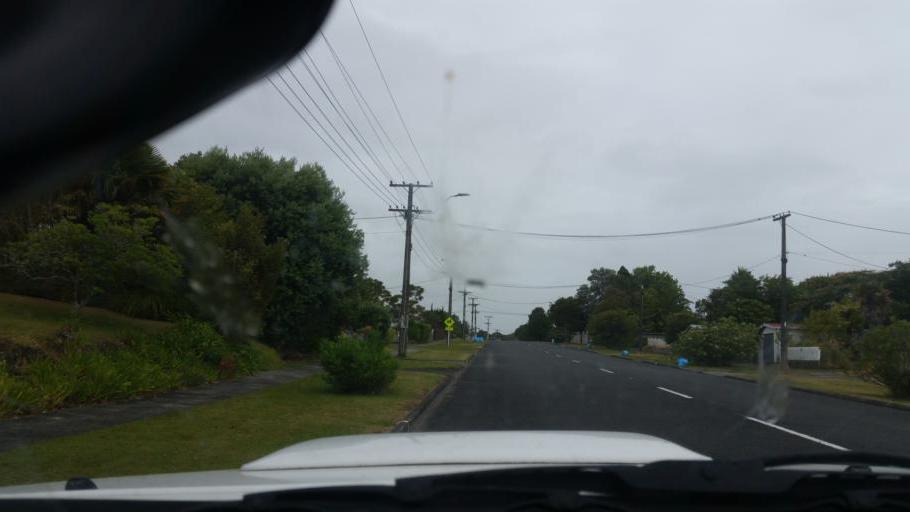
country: NZ
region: Northland
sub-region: Kaipara District
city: Dargaville
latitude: -35.9354
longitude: 173.8653
